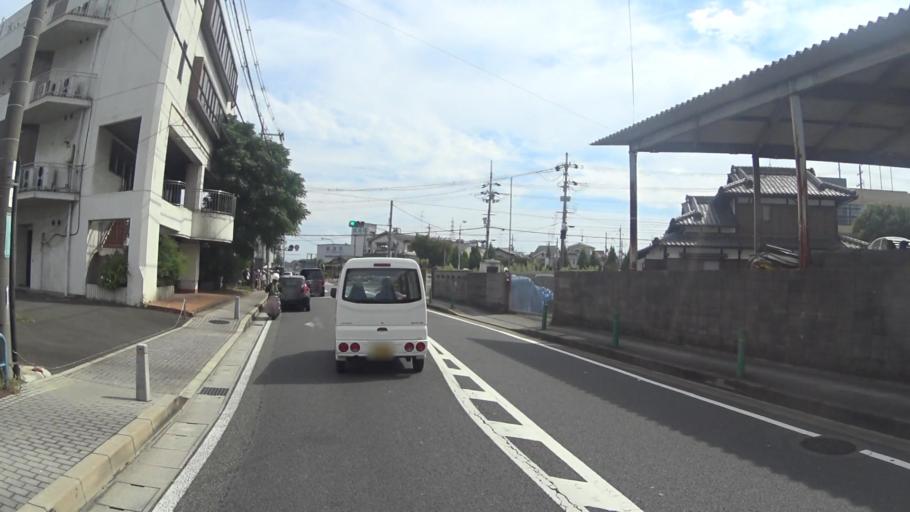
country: JP
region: Kyoto
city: Yawata
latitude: 34.8635
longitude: 135.7067
